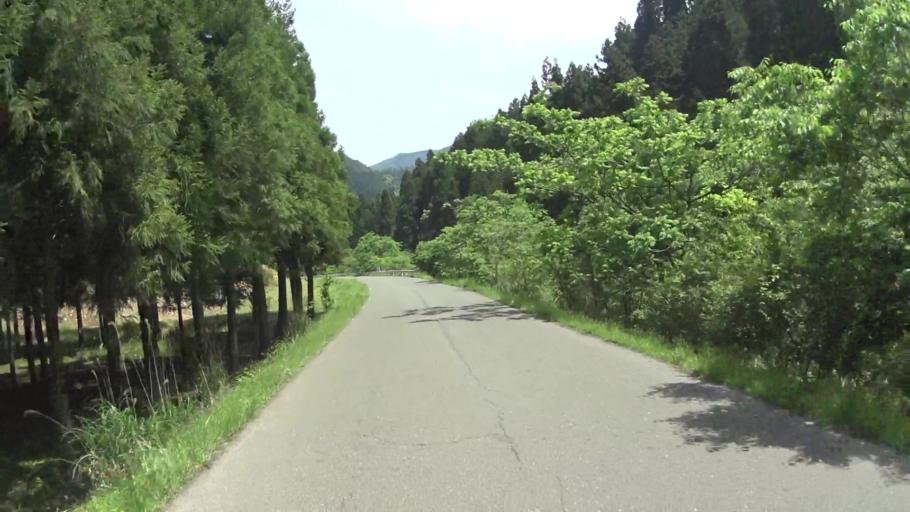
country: JP
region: Kyoto
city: Maizuru
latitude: 35.4401
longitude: 135.5123
